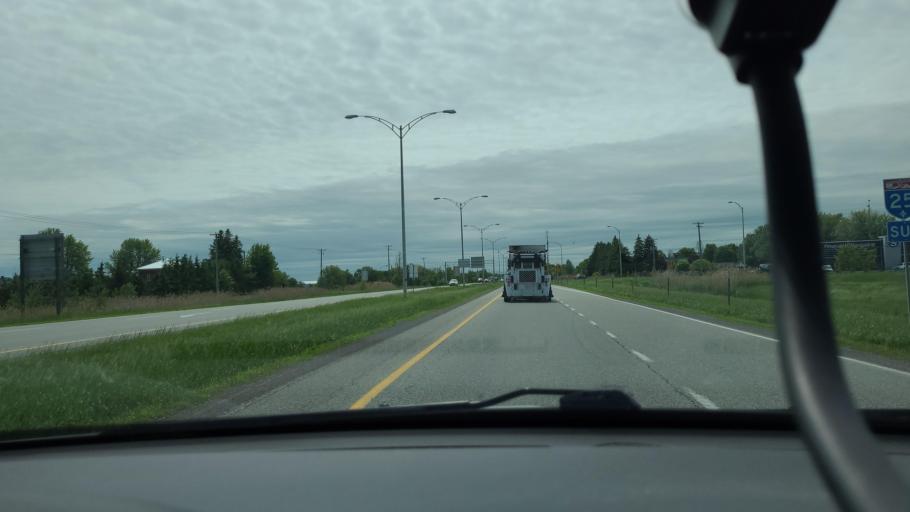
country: CA
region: Quebec
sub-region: Lanaudiere
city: Sainte-Julienne
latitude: 45.9027
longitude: -73.6592
